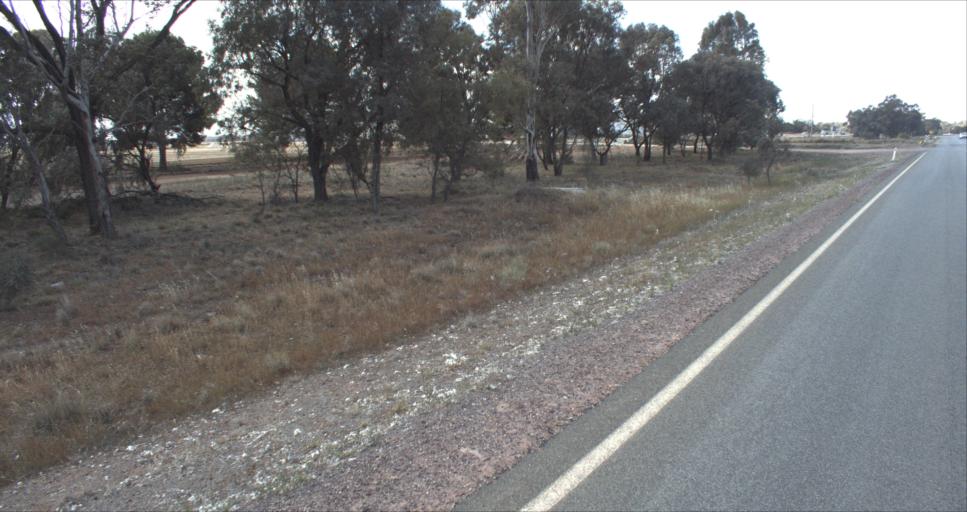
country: AU
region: New South Wales
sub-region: Murrumbidgee Shire
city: Darlington Point
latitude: -34.5914
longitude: 146.1635
